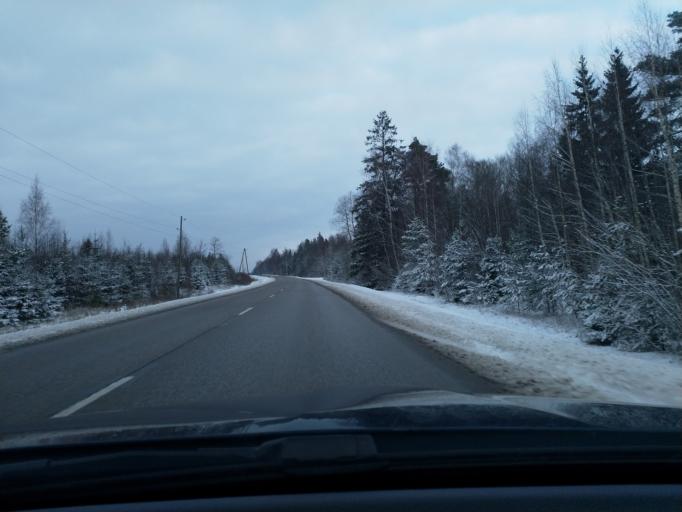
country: LV
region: Kuldigas Rajons
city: Kuldiga
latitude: 56.9340
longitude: 21.9263
